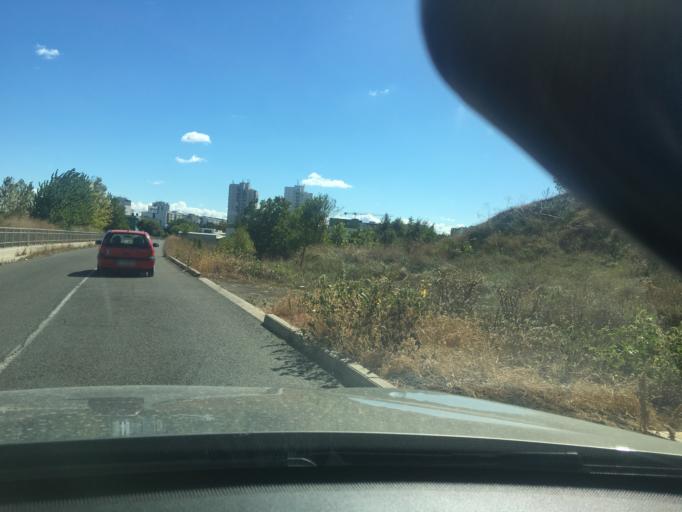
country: BG
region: Burgas
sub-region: Obshtina Burgas
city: Burgas
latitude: 42.5317
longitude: 27.4534
